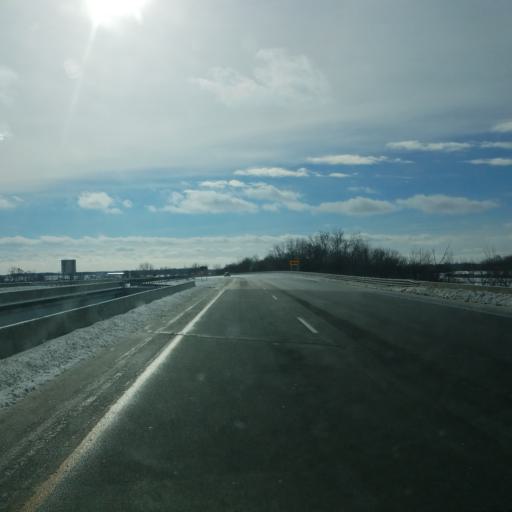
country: US
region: Michigan
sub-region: Gratiot County
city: Ithaca
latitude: 43.2876
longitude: -84.5823
